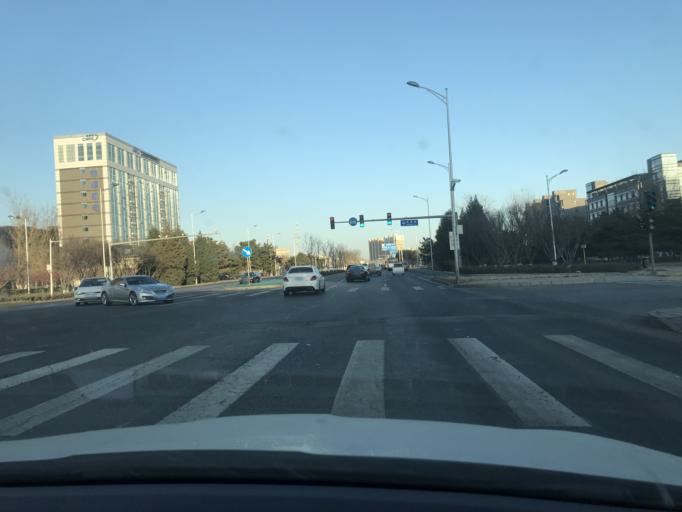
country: CN
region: Beijing
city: Xibeiwang
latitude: 40.0741
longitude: 116.2443
